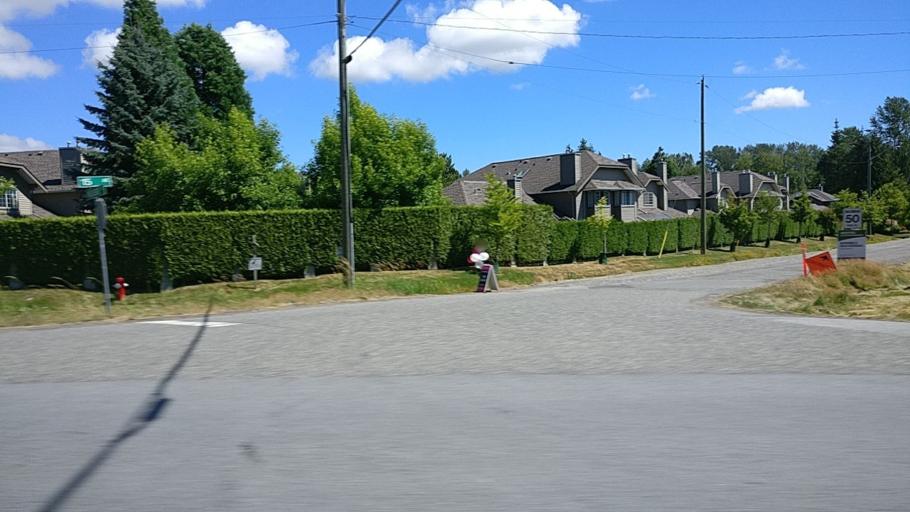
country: CA
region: British Columbia
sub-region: Greater Vancouver Regional District
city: White Rock
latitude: 49.0292
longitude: -122.7733
